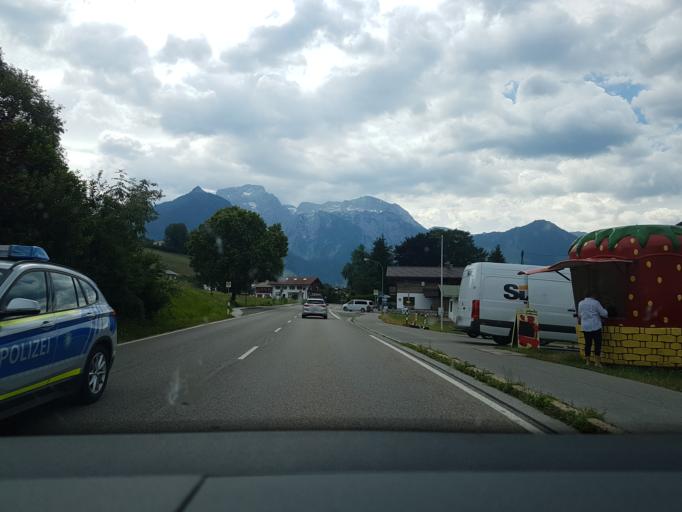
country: DE
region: Bavaria
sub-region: Upper Bavaria
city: Berchtesgaden
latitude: 47.6344
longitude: 12.9780
